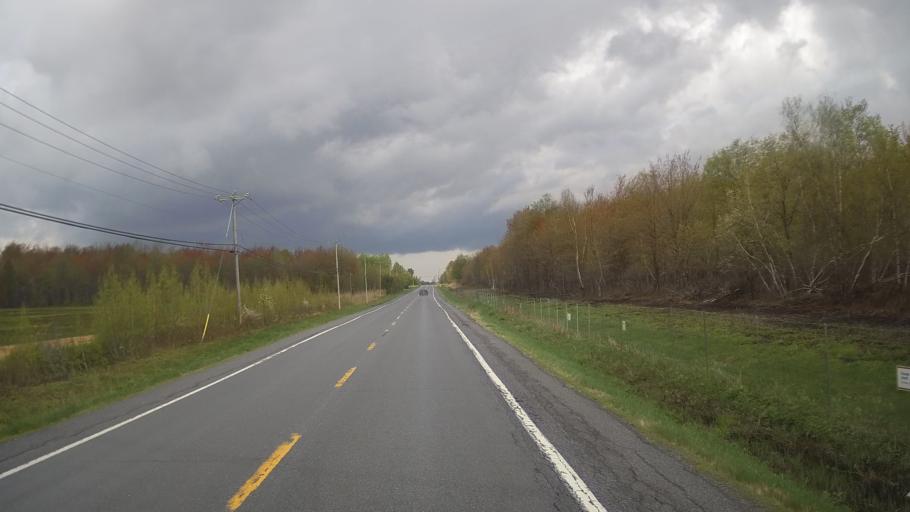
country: CA
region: Quebec
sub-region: Monteregie
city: Farnham
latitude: 45.3021
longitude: -73.0346
